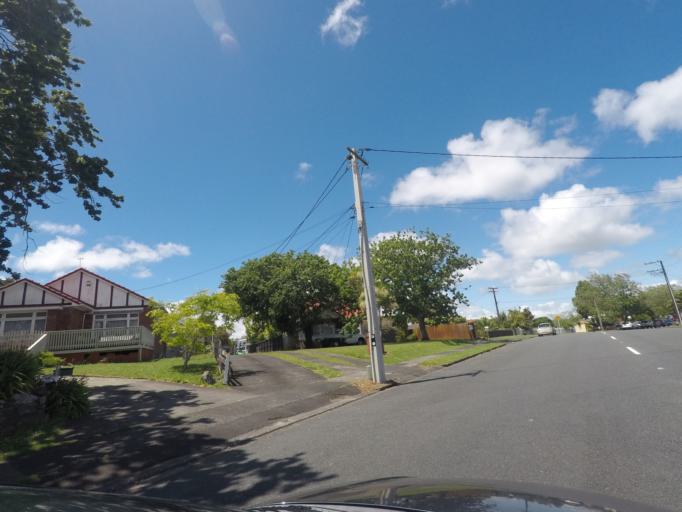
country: NZ
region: Auckland
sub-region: Auckland
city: Rosebank
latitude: -36.8841
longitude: 174.6438
